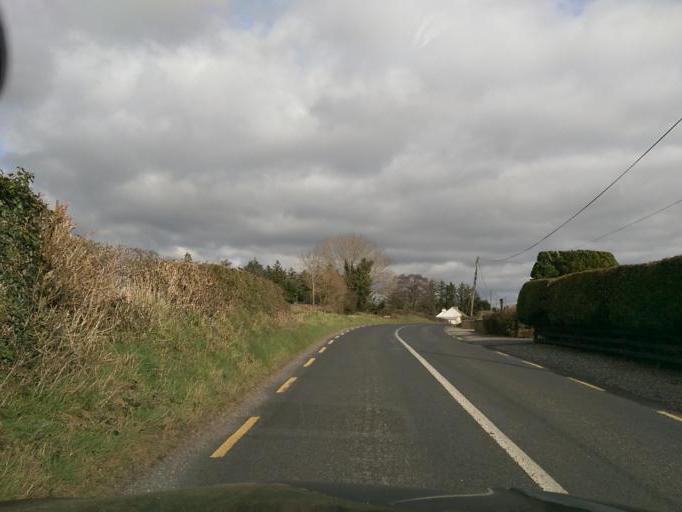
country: IE
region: Connaught
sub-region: County Galway
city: Ballinasloe
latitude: 53.3290
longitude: -8.2991
